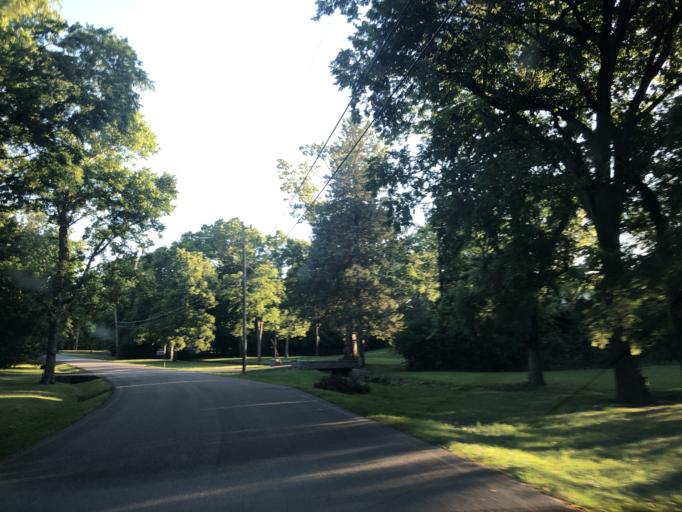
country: US
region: Tennessee
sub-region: Davidson County
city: Oak Hill
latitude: 36.0847
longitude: -86.8018
